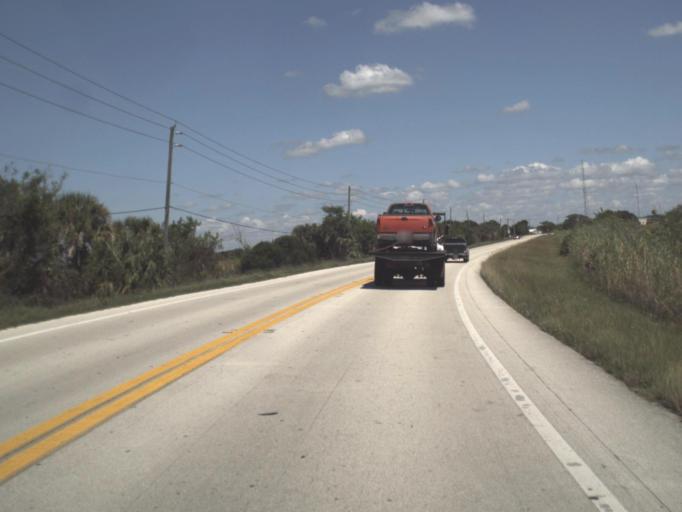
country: US
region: Florida
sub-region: Okeechobee County
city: Okeechobee
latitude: 27.1888
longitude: -80.8509
